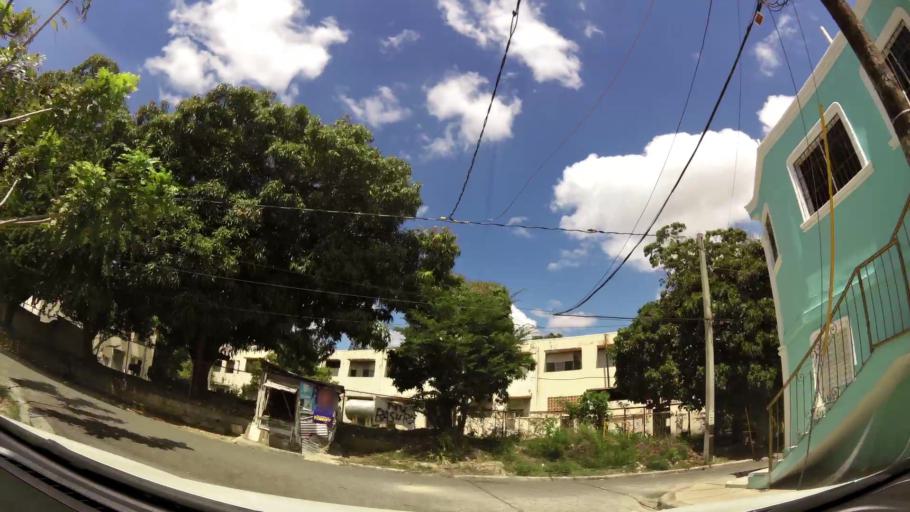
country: DO
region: San Cristobal
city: San Cristobal
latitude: 18.4085
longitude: -70.1158
